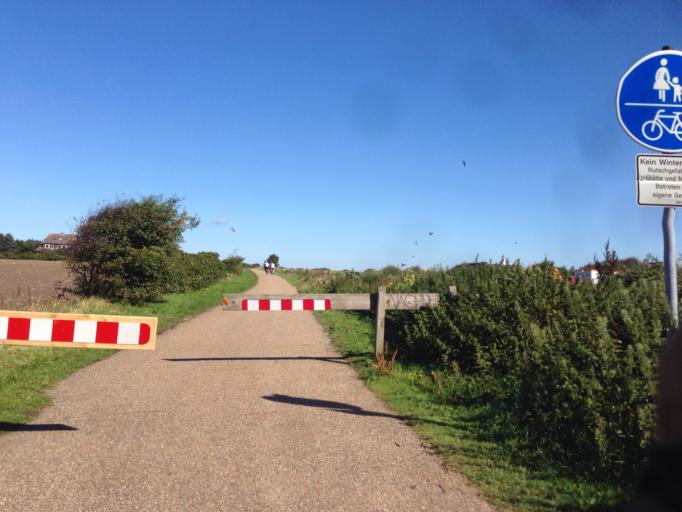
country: DE
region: Schleswig-Holstein
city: Tinnum
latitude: 54.9391
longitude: 8.3308
